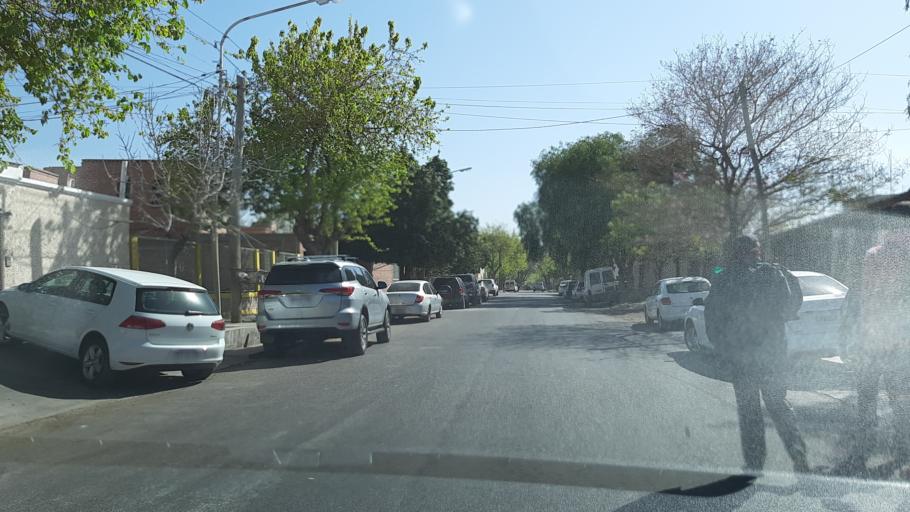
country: AR
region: San Juan
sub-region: Departamento de Santa Lucia
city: Santa Lucia
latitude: -31.5353
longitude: -68.5119
